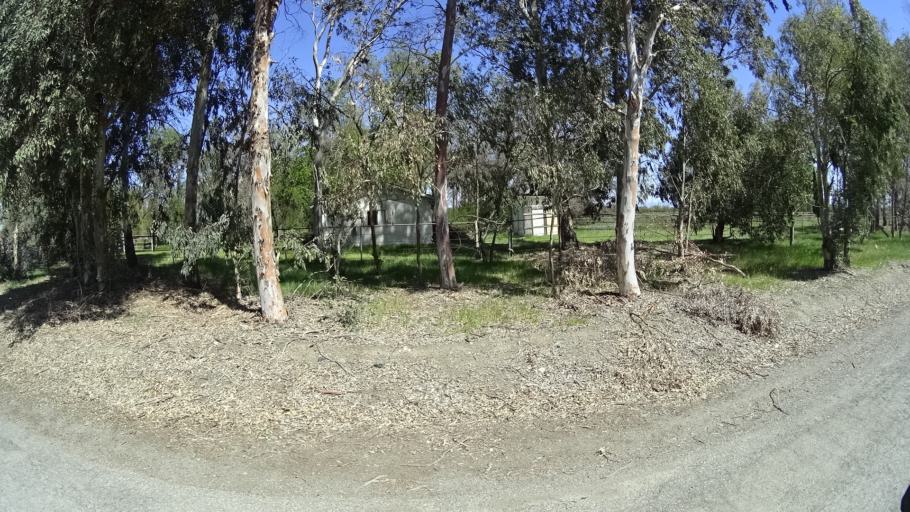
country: US
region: California
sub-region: Glenn County
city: Orland
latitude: 39.7863
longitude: -122.2758
